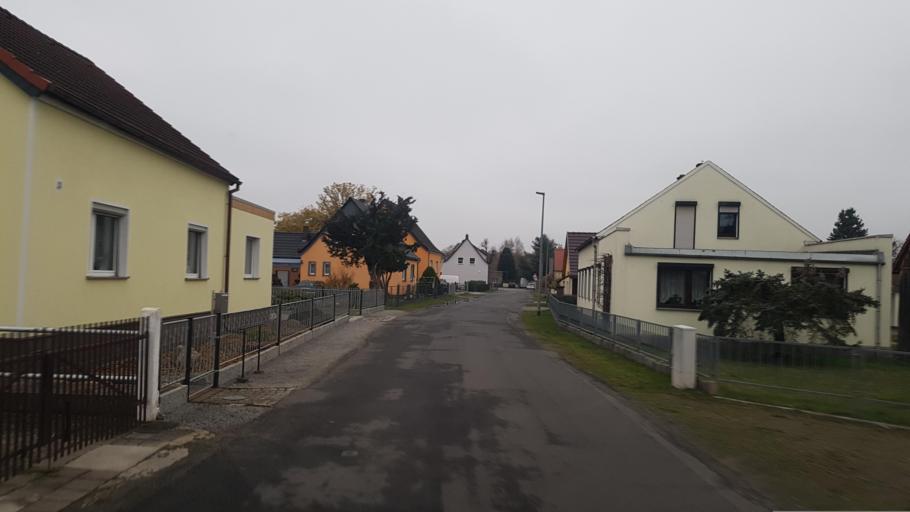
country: DE
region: Brandenburg
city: Ruhland
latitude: 51.4300
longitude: 13.8597
